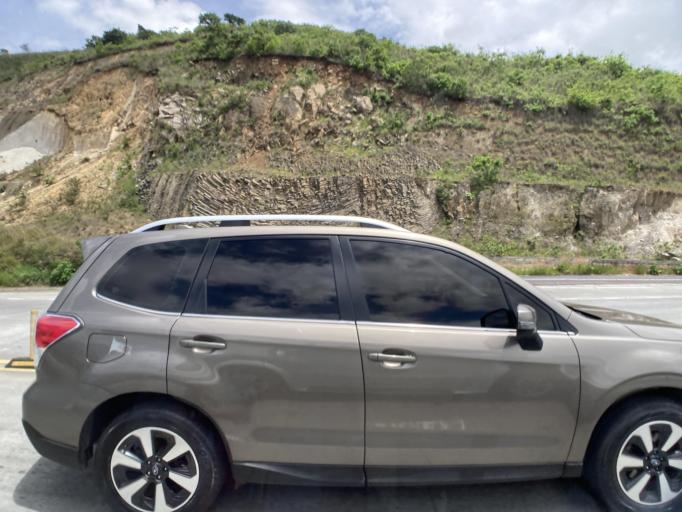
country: GT
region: Guatemala
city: Amatitlan
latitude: 14.4916
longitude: -90.5963
